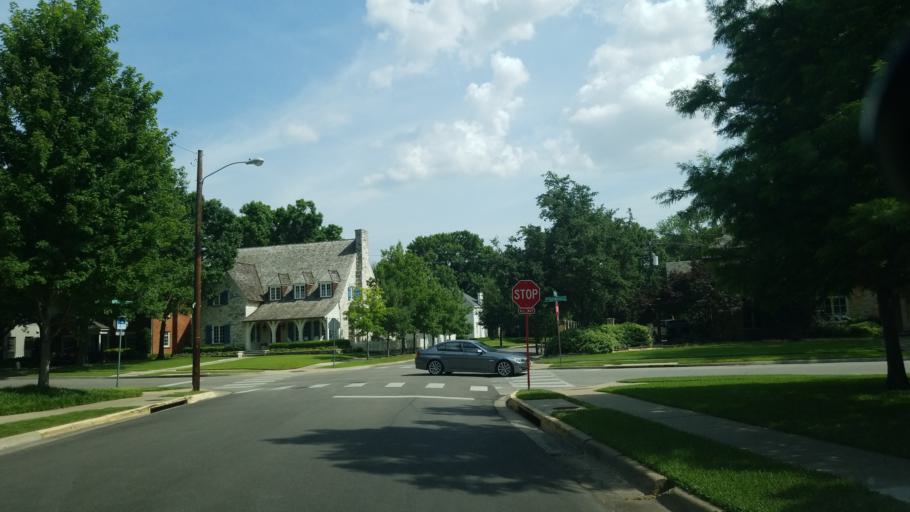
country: US
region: Texas
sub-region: Dallas County
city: University Park
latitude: 32.8573
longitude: -96.7894
